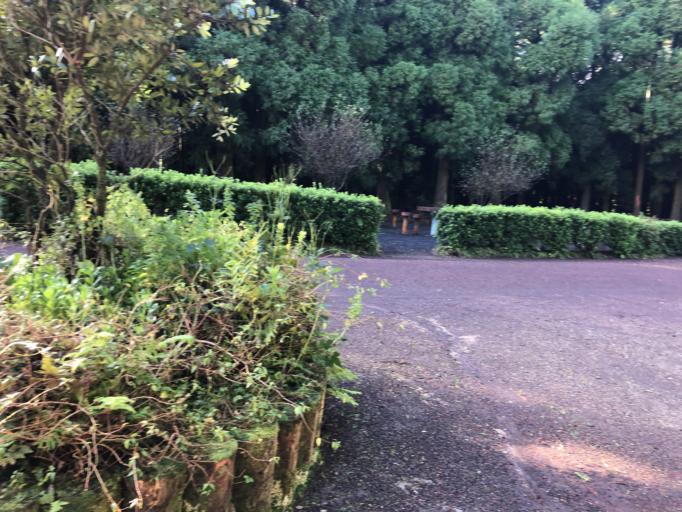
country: PT
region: Azores
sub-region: Ponta Delgada
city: Arrifes
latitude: 37.8378
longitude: -25.7574
